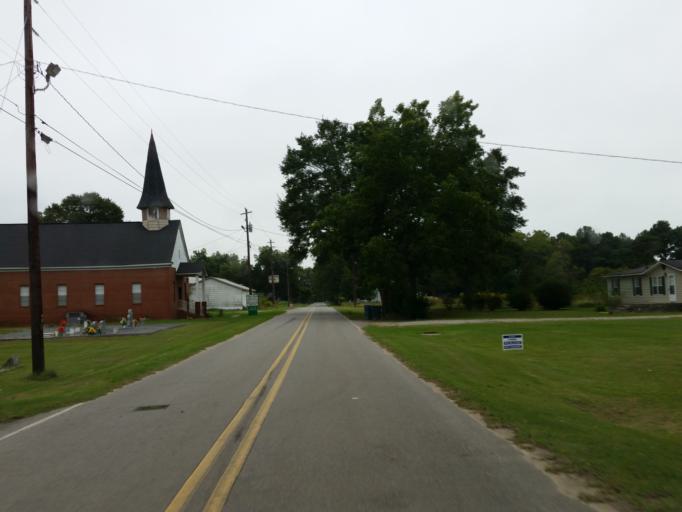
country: US
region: Georgia
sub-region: Dooly County
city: Unadilla
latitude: 32.2676
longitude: -83.7388
